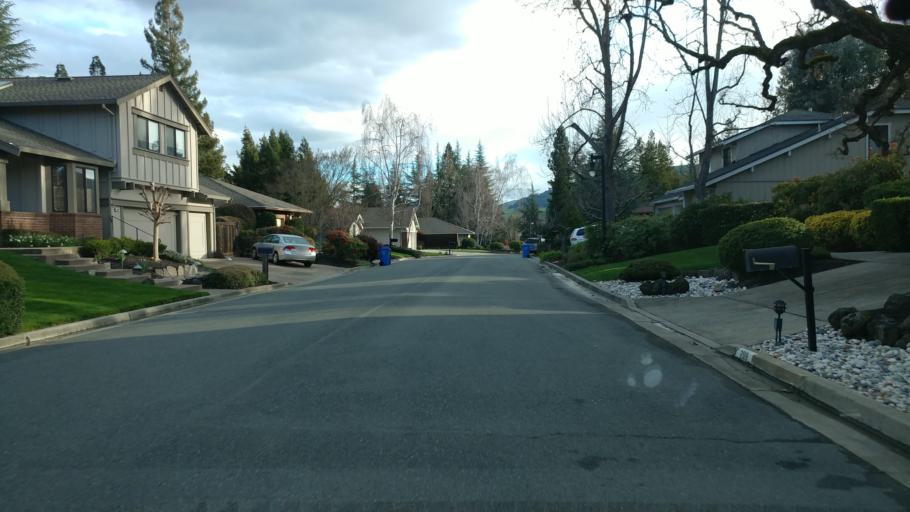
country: US
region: California
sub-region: Contra Costa County
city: Danville
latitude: 37.8295
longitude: -121.9924
